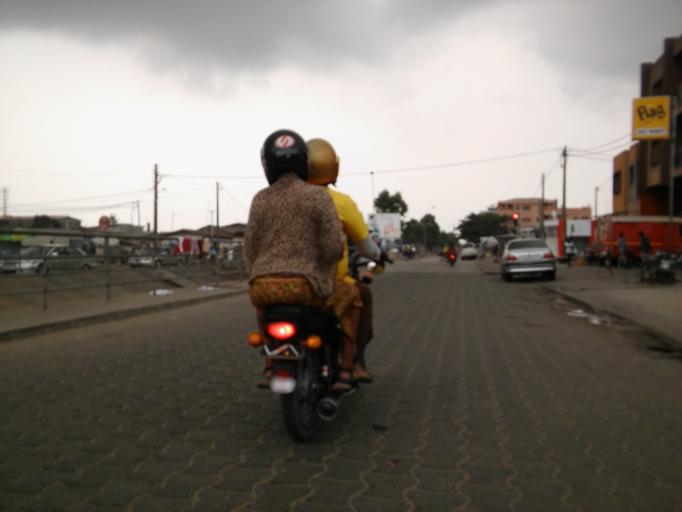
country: BJ
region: Littoral
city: Cotonou
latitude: 6.3751
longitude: 2.4142
